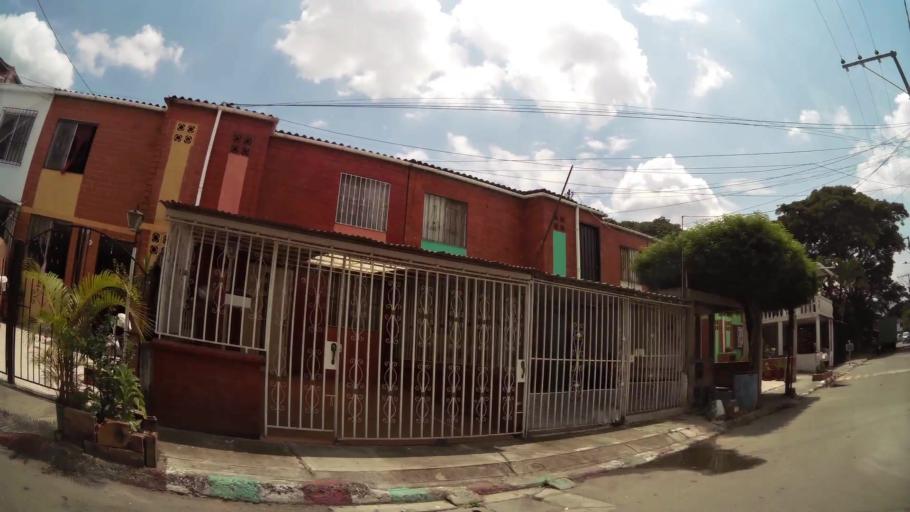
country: CO
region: Valle del Cauca
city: Cali
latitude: 3.4554
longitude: -76.4689
